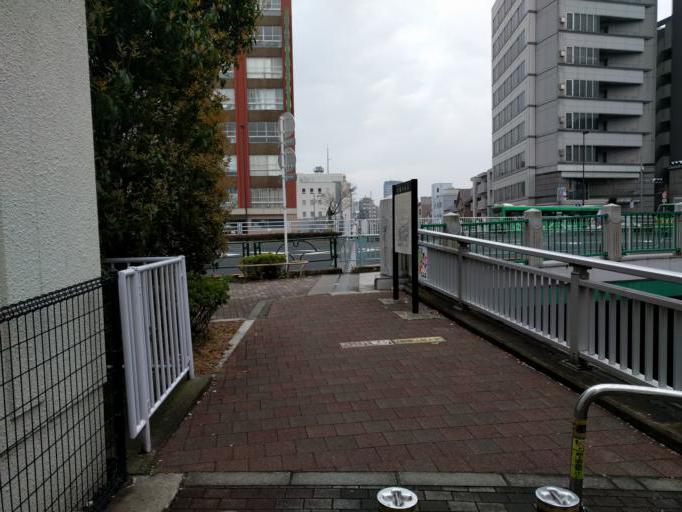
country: JP
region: Tokyo
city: Tokyo
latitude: 35.6967
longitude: 139.6868
